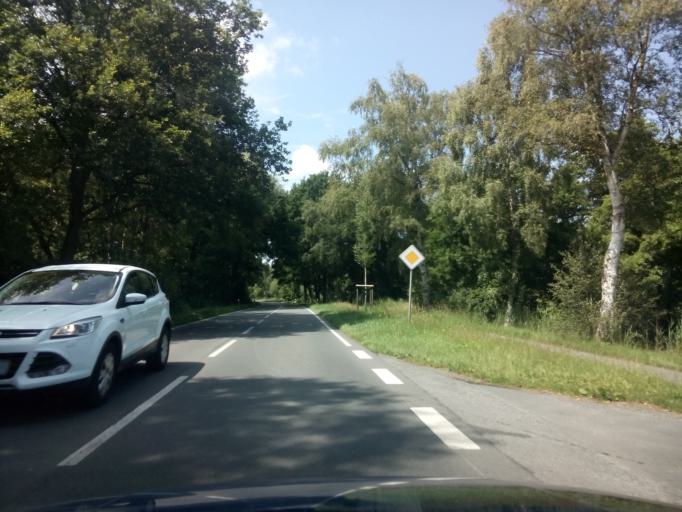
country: DE
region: Lower Saxony
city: Osterholz-Scharmbeck
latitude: 53.2529
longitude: 8.8426
